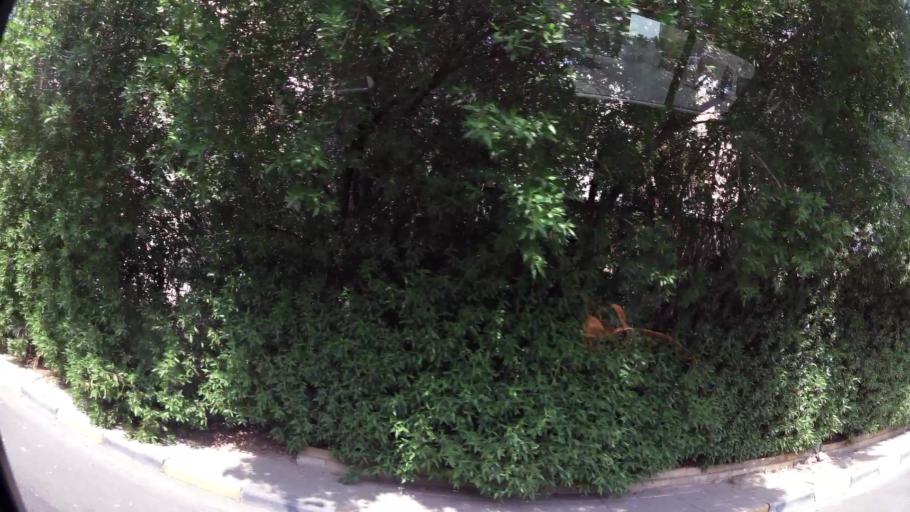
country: KW
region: Muhafazat al Jahra'
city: Al Jahra'
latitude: 29.3187
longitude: 47.6731
